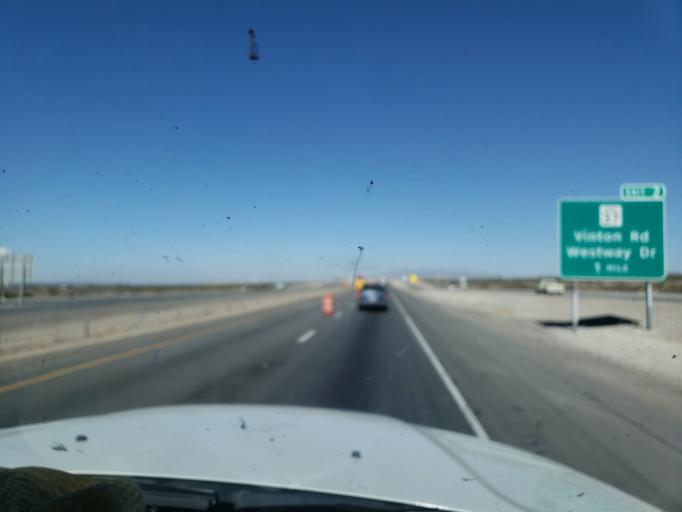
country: US
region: Texas
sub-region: El Paso County
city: Westway
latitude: 31.9351
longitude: -106.5827
